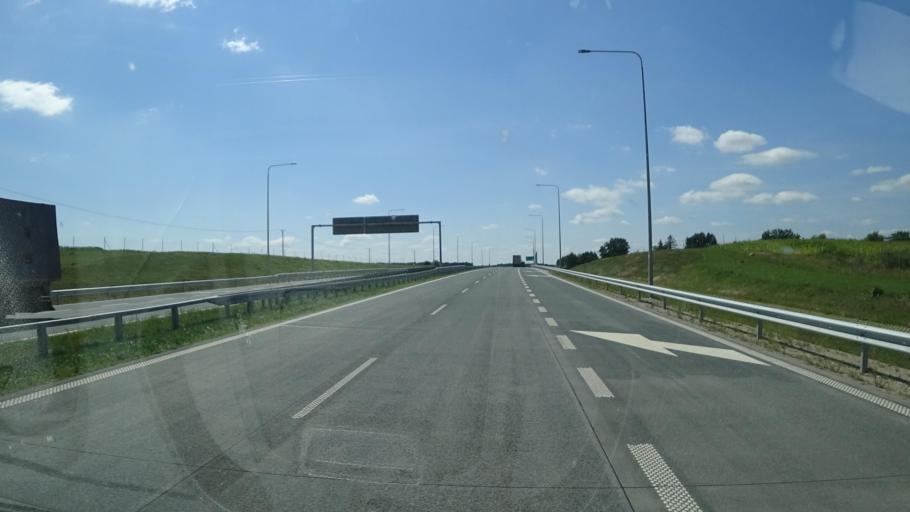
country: PL
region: Podlasie
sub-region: Powiat kolnenski
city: Stawiski
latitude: 53.4553
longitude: 22.1946
